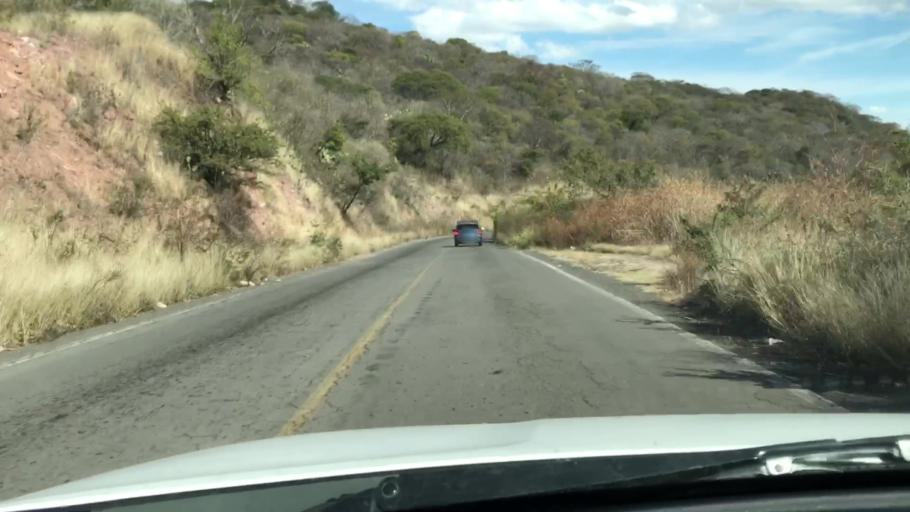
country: MX
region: Jalisco
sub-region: Zacoalco de Torres
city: Barranca de Otates (Barranca de Otatan)
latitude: 20.2469
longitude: -103.6772
